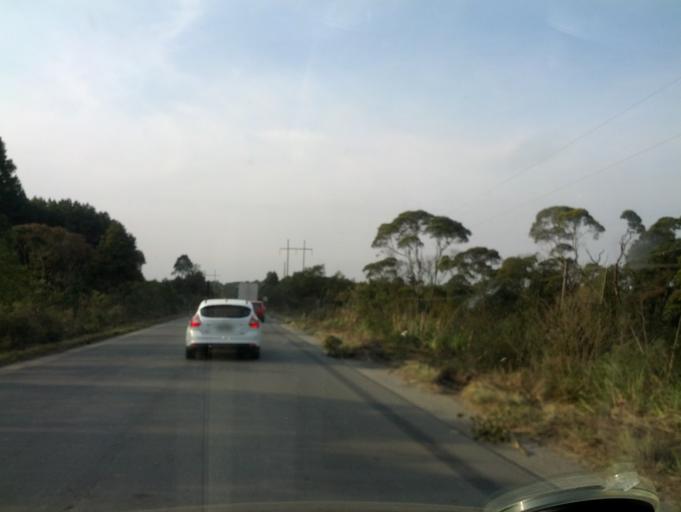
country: BR
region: Santa Catarina
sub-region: Otacilio Costa
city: Otacilio Costa
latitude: -27.5411
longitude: -50.1450
